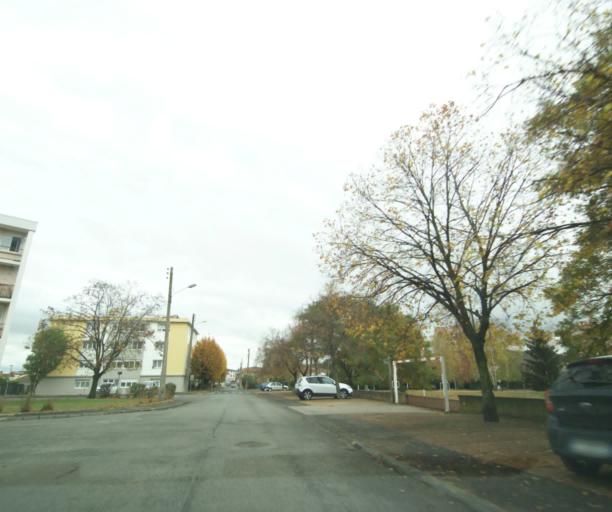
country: FR
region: Auvergne
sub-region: Departement du Puy-de-Dome
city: Pont-du-Chateau
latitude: 45.8015
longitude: 3.2452
